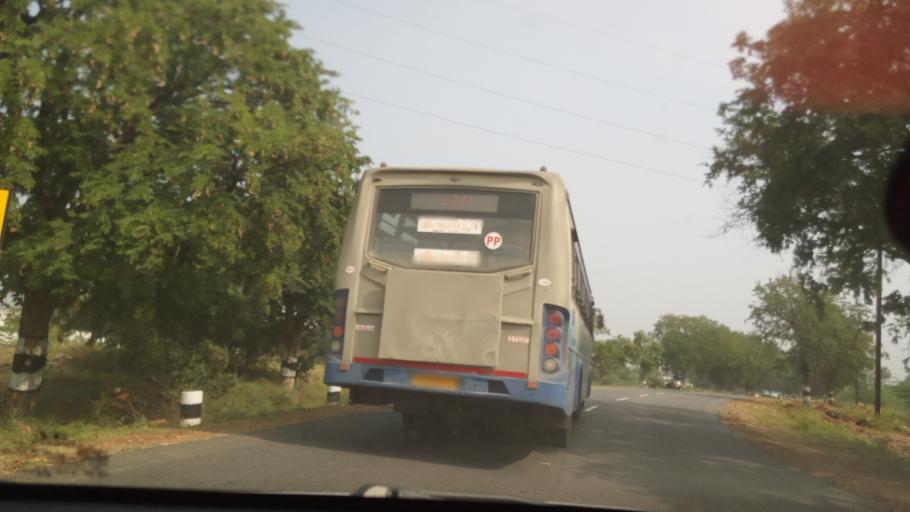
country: IN
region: Tamil Nadu
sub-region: Erode
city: Punjai Puliyampatti
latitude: 11.4221
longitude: 77.1938
